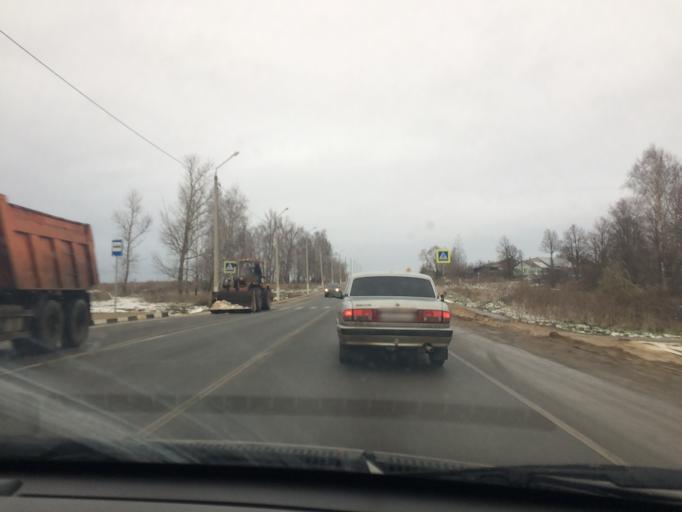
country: RU
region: Tula
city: Gorelki
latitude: 54.2377
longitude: 37.6583
